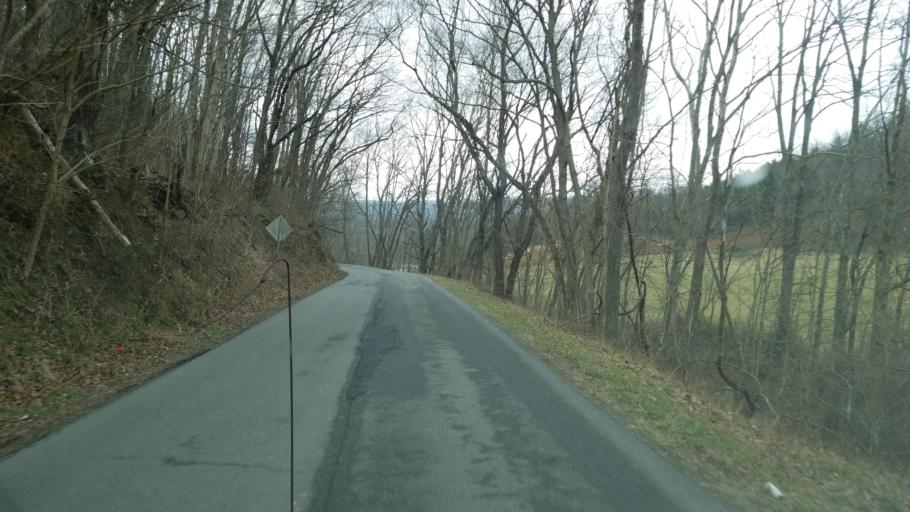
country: US
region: Virginia
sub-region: Giles County
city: Pembroke
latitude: 37.2481
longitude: -80.6831
